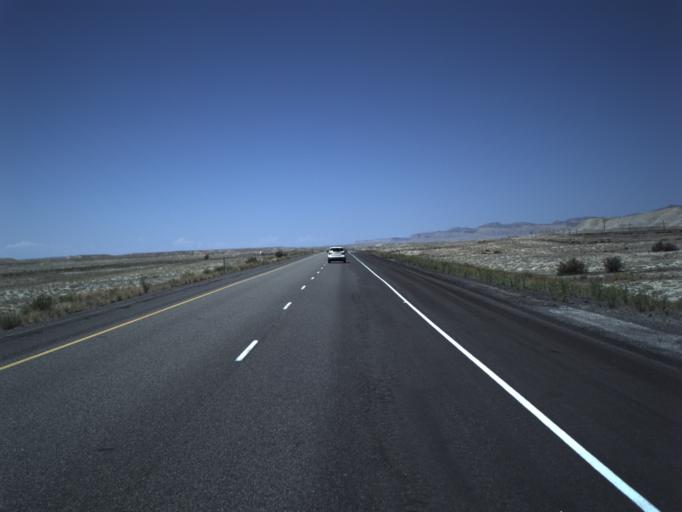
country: US
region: Utah
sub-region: Grand County
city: Moab
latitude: 38.9346
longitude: -109.4491
